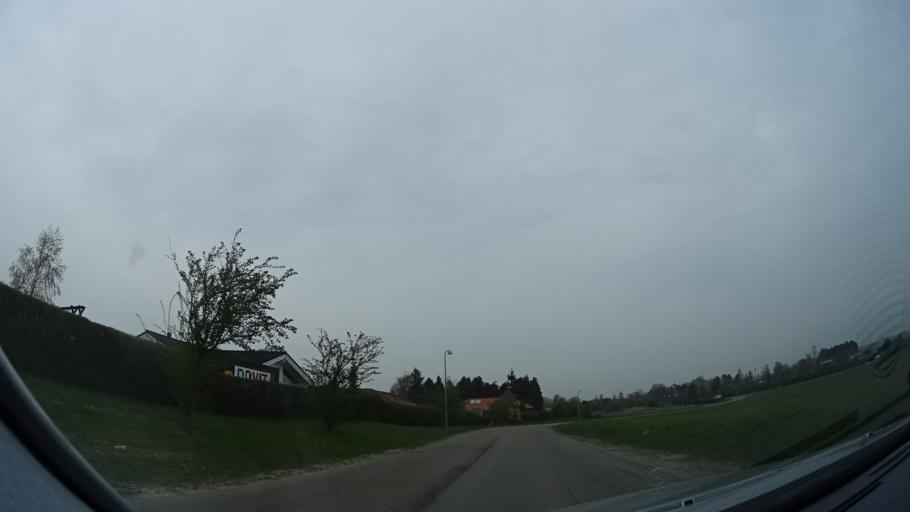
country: DK
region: Zealand
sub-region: Lejre Kommune
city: Ejby
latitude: 55.7010
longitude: 11.9008
